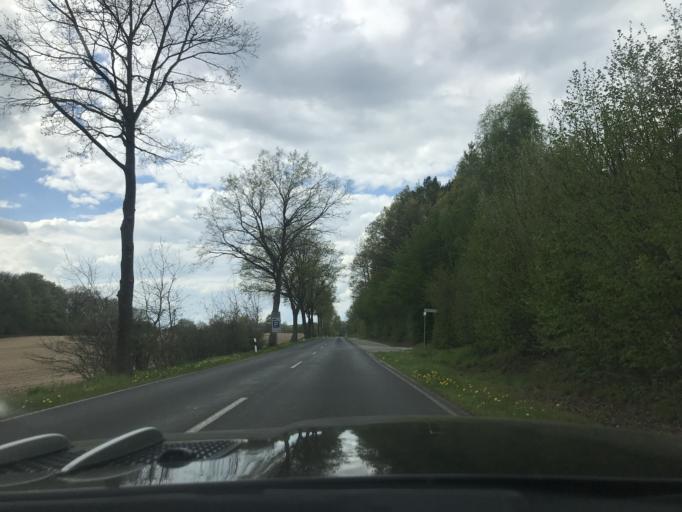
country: DE
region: Schleswig-Holstein
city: Gross Gronau
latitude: 53.7850
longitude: 10.7619
